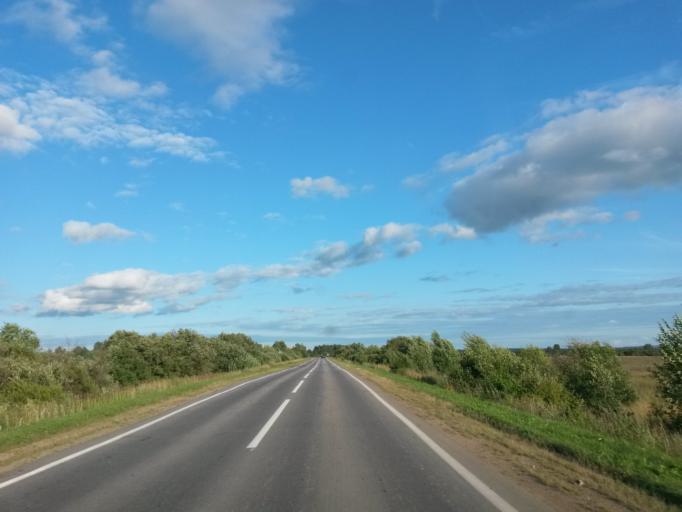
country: RU
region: Jaroslavl
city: Konstantinovskiy
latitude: 57.8516
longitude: 39.6262
